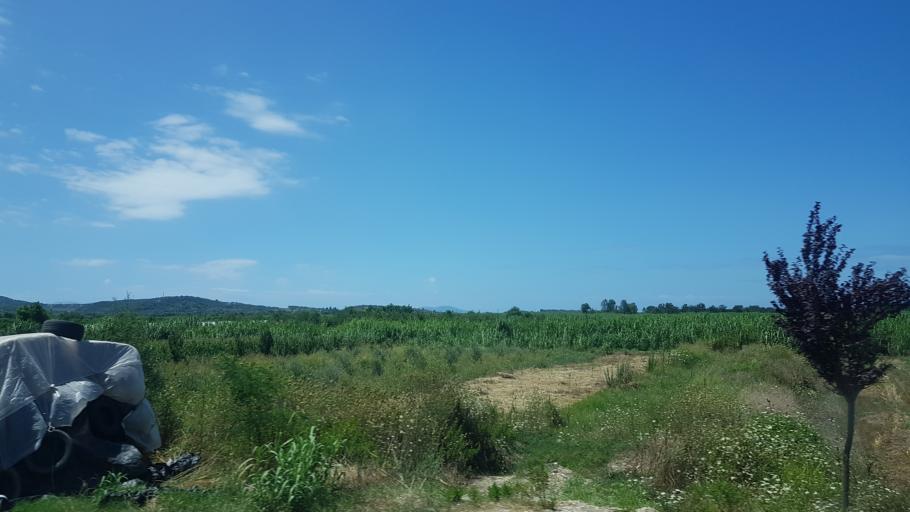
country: AL
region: Fier
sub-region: Rrethi i Fierit
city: Frakulla e Madhe
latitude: 40.6220
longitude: 19.5159
